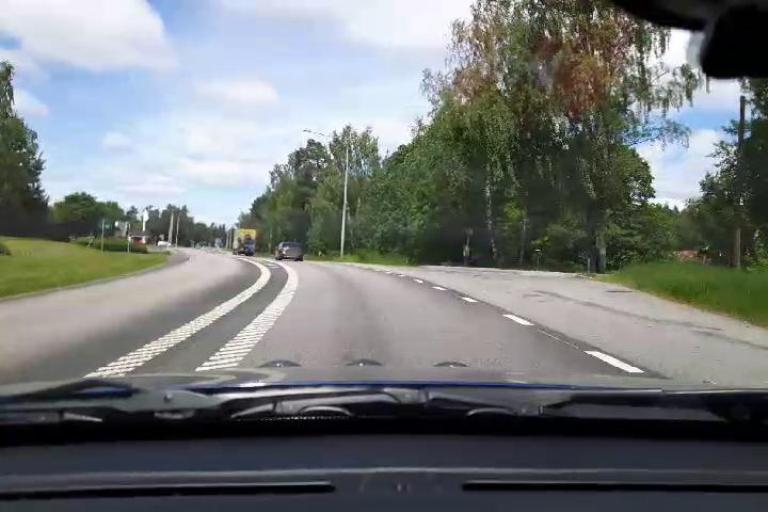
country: SE
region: Uppsala
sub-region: Osthammars Kommun
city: Bjorklinge
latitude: 60.0283
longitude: 17.5536
